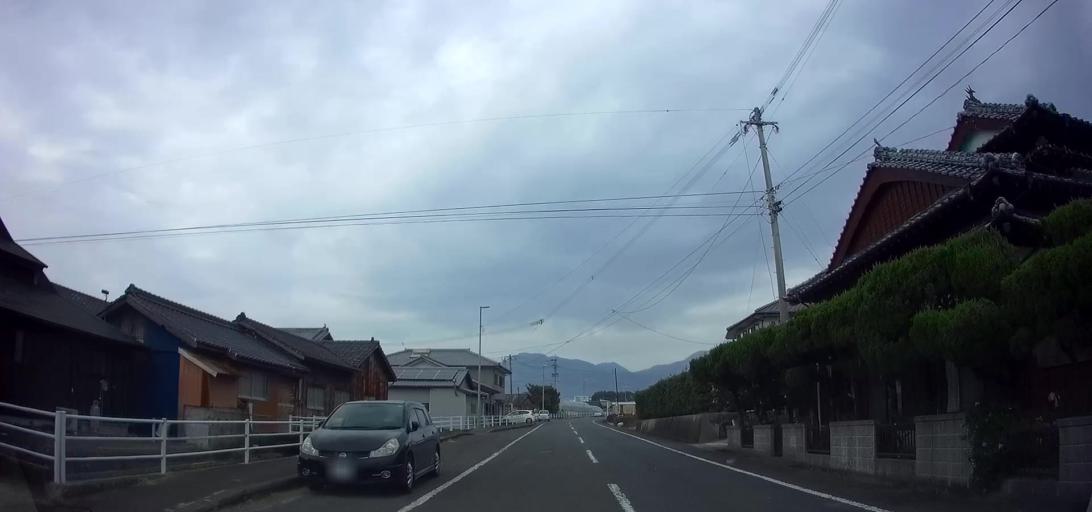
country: JP
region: Nagasaki
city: Shimabara
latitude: 32.6594
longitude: 130.3111
